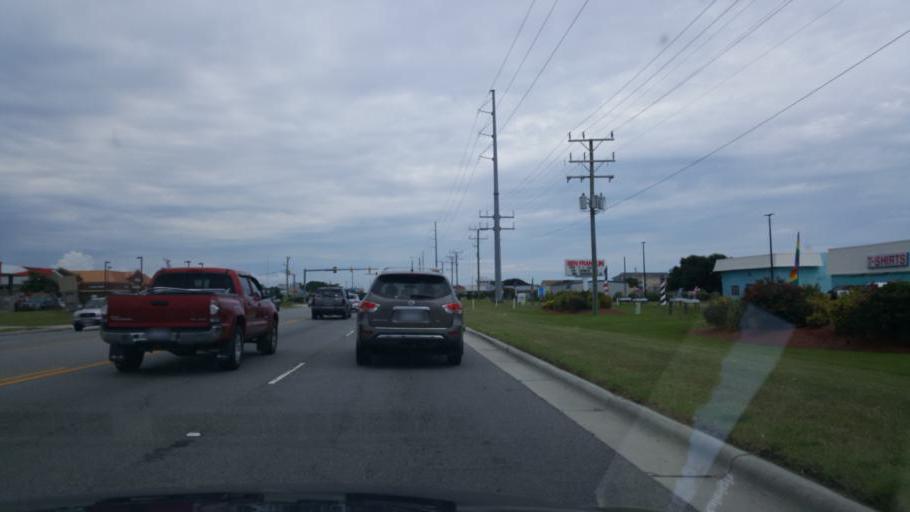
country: US
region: North Carolina
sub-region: Dare County
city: Nags Head
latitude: 35.9918
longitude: -75.6477
